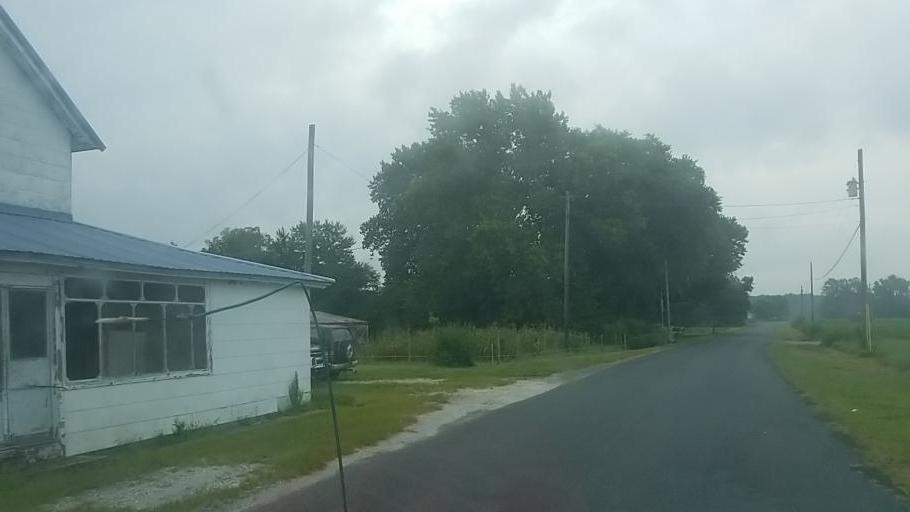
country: US
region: Maryland
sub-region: Wicomico County
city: Pittsville
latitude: 38.4502
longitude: -75.3524
